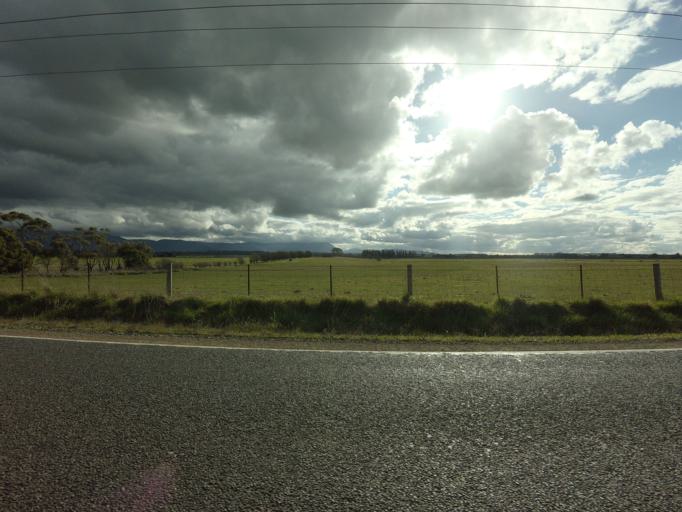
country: AU
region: Tasmania
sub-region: Northern Midlands
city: Longford
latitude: -41.7412
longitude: 147.0824
